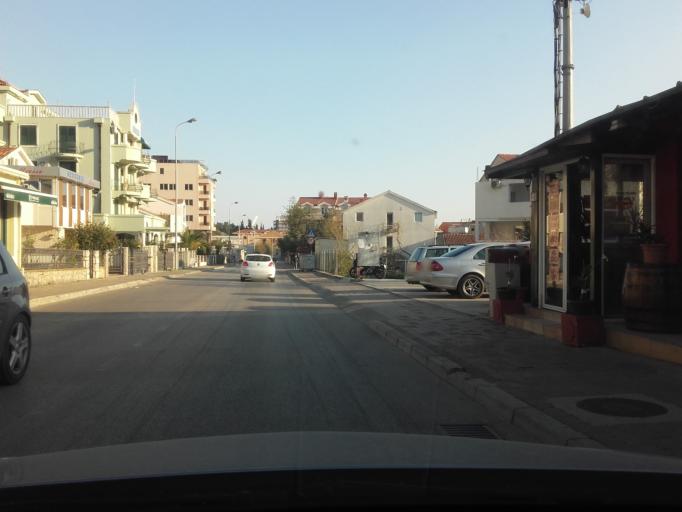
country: ME
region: Budva
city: Budva
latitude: 42.2900
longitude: 18.8510
